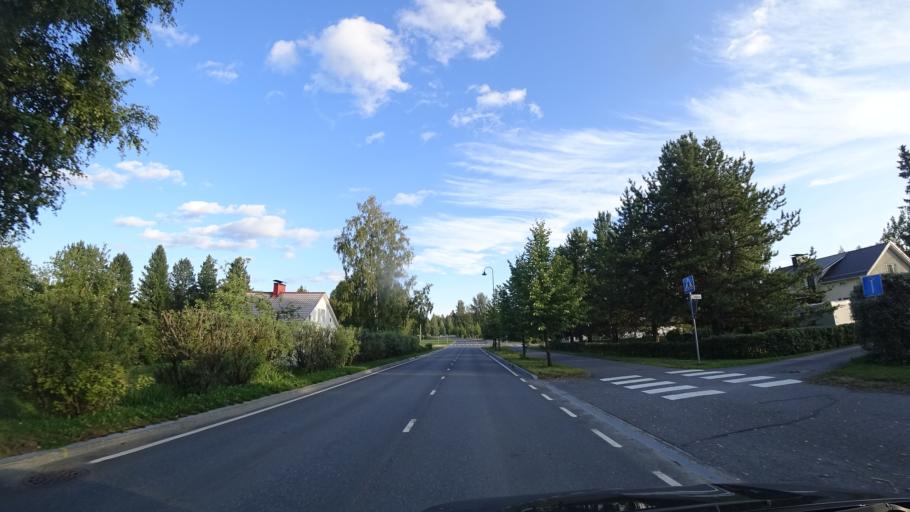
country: FI
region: Haeme
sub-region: Haemeenlinna
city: Lammi
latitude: 61.0756
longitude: 25.0110
